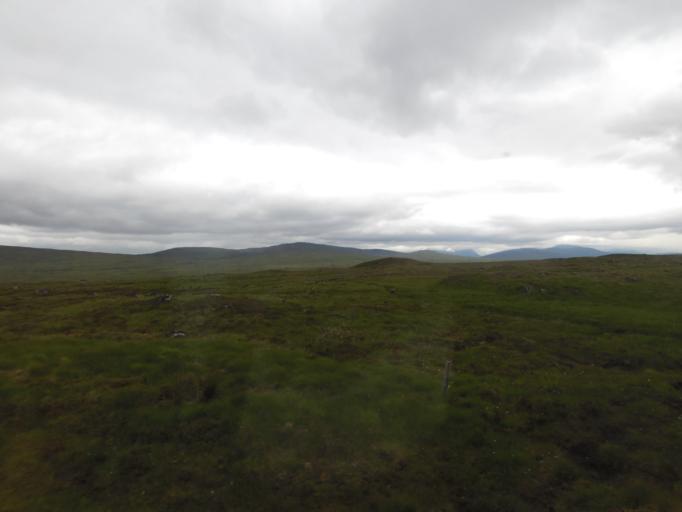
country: GB
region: Scotland
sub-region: Highland
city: Spean Bridge
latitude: 56.7234
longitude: -4.6318
